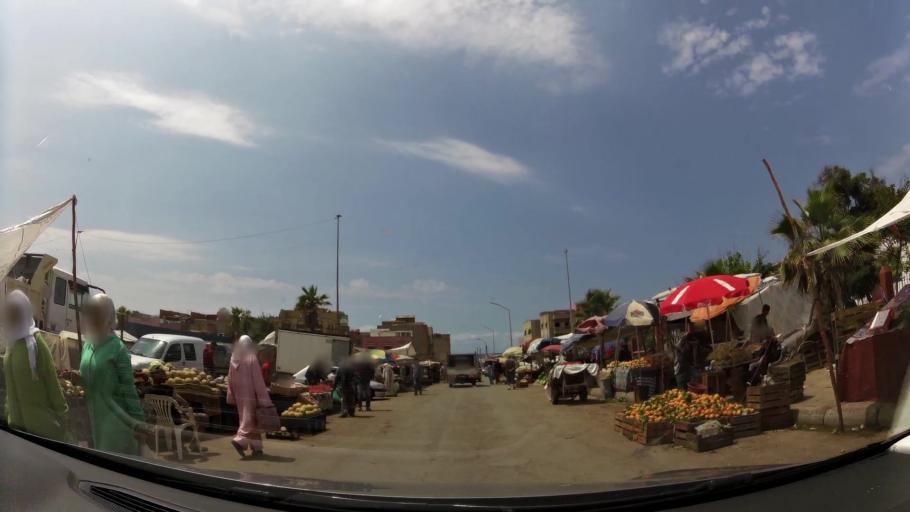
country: MA
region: Rabat-Sale-Zemmour-Zaer
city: Sale
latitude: 34.0540
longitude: -6.8184
